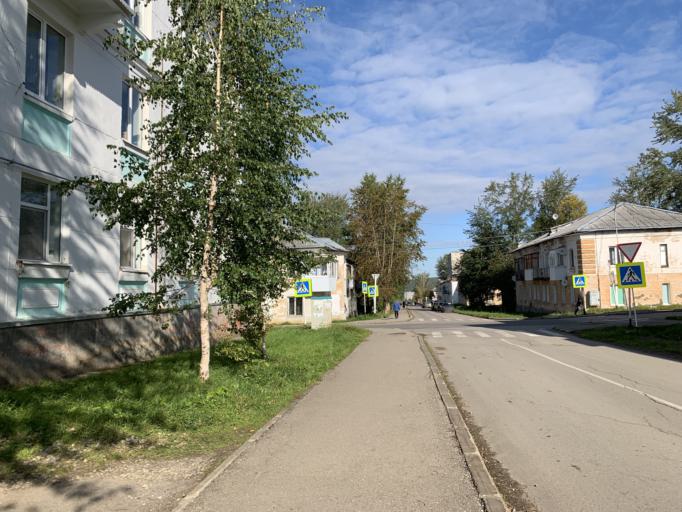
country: RU
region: Perm
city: Gubakha
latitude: 58.8402
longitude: 57.5552
